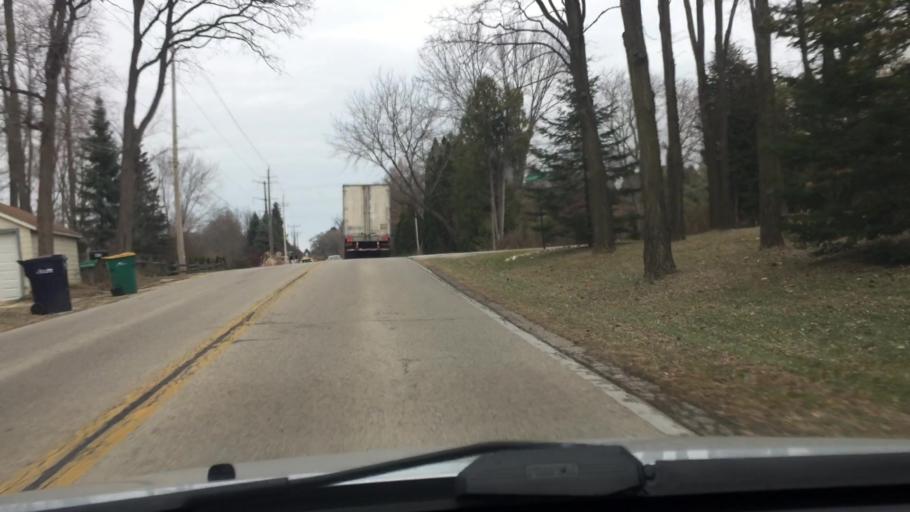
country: US
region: Wisconsin
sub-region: Ozaukee County
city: Cedarburg
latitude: 43.2898
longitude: -87.9666
